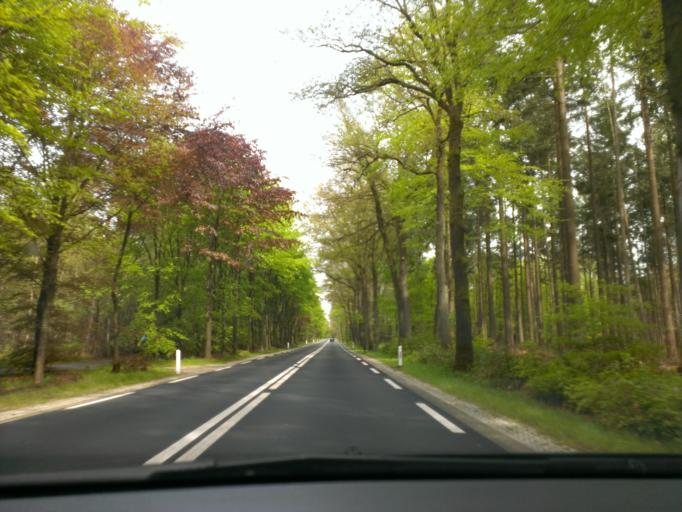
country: NL
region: Gelderland
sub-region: Gemeente Oldebroek
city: Oldebroek
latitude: 52.3573
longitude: 5.8797
